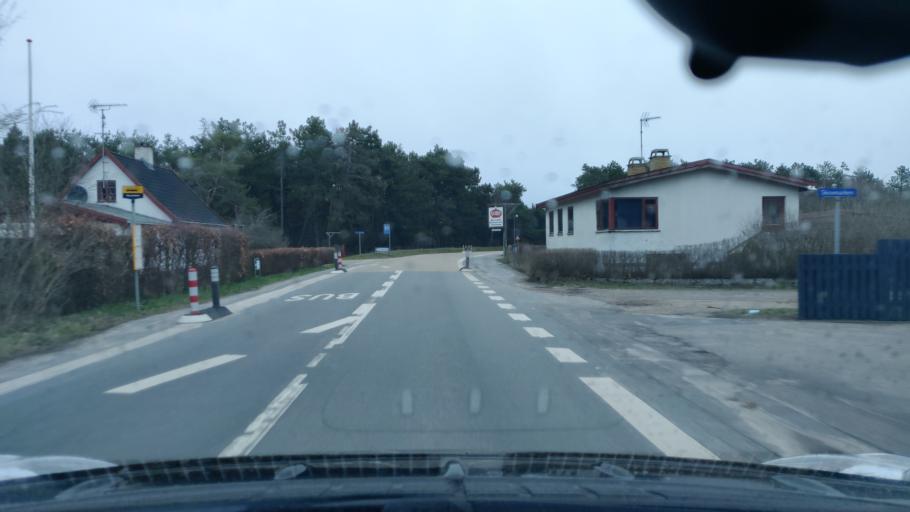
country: DK
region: Zealand
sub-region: Odsherred Kommune
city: Hojby
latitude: 55.8846
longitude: 11.5502
